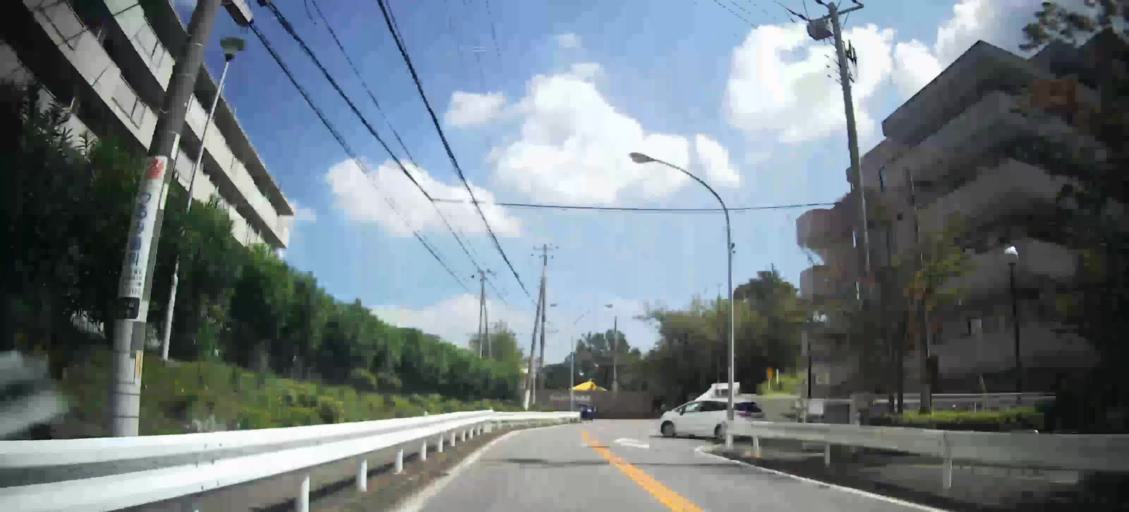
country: JP
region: Kanagawa
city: Yokohama
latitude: 35.4540
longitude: 139.5599
